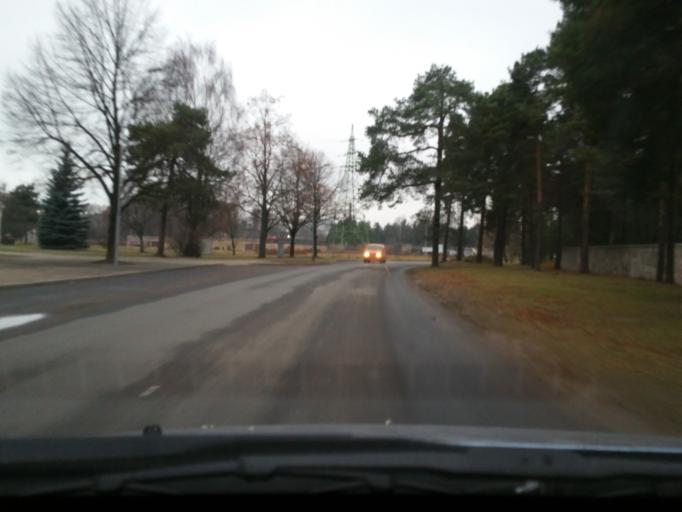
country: LV
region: Riga
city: Riga
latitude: 56.9871
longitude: 24.1429
